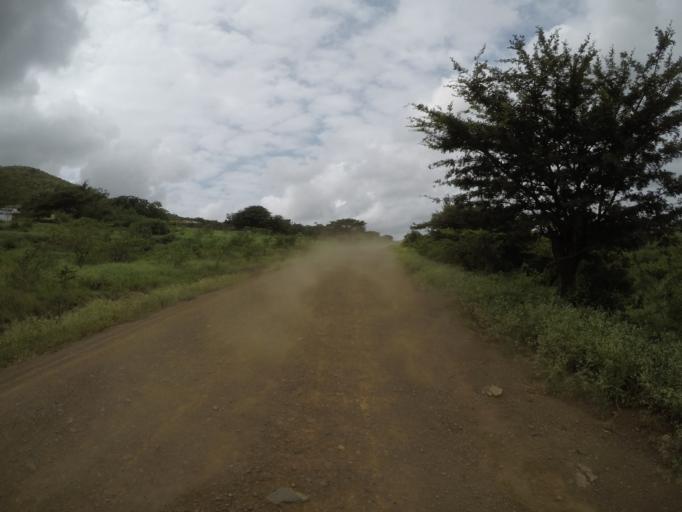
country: ZA
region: KwaZulu-Natal
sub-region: uThungulu District Municipality
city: Empangeni
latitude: -28.6047
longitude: 31.8943
